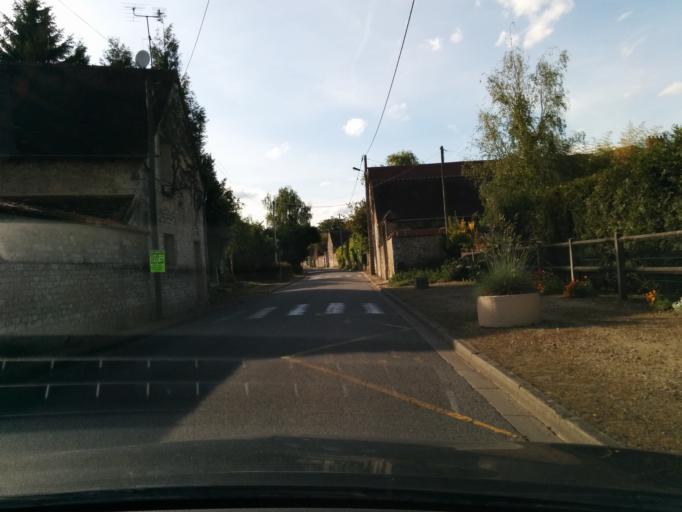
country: FR
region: Haute-Normandie
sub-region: Departement de l'Eure
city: Courcelles-sur-Seine
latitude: 49.1652
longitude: 1.4126
